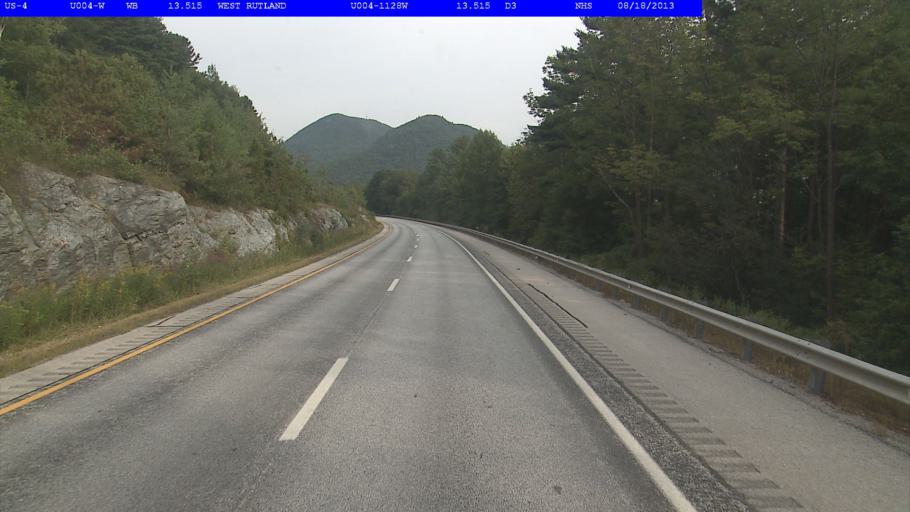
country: US
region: Vermont
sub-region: Rutland County
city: West Rutland
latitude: 43.5996
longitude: -73.0582
